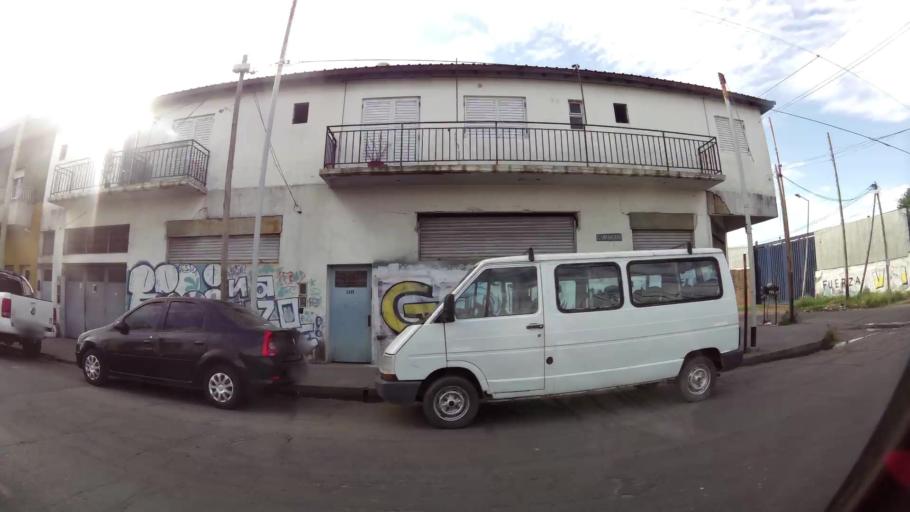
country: AR
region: Buenos Aires
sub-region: Partido de Lanus
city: Lanus
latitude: -34.7117
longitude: -58.3503
